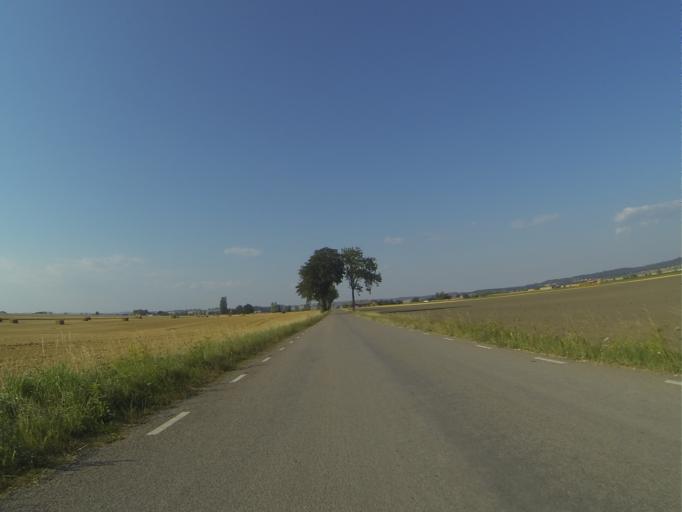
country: SE
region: Skane
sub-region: Lunds Kommun
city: Genarp
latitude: 55.6041
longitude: 13.3660
